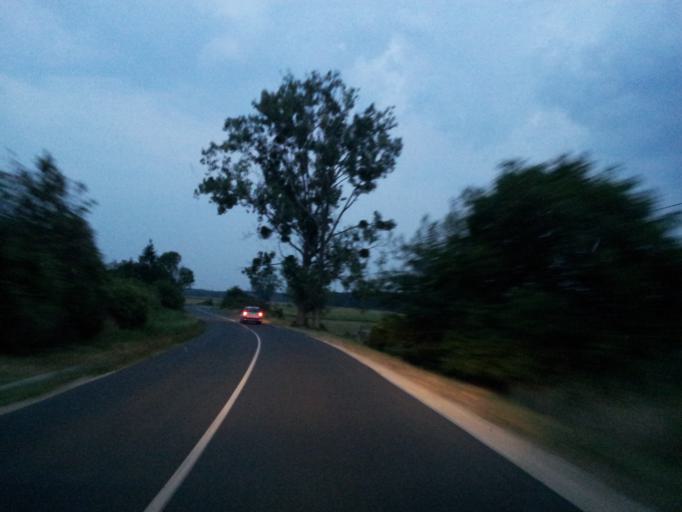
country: HU
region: Veszprem
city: Sumeg
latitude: 46.9708
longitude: 17.3074
